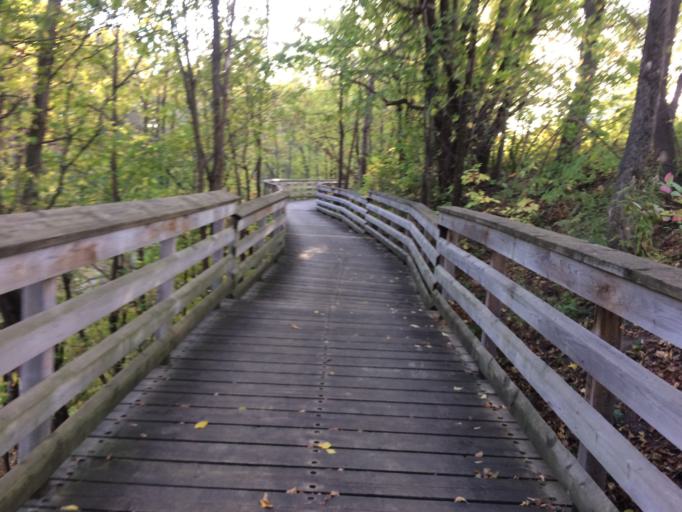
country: CA
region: Quebec
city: Quebec
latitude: 46.8088
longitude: -71.2574
